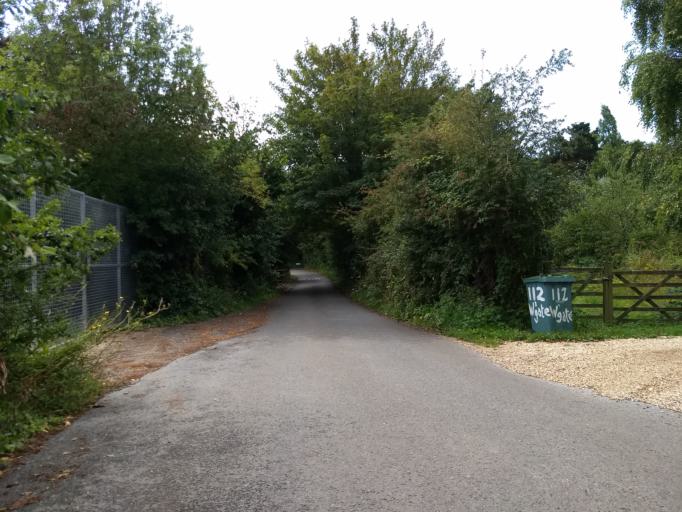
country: GB
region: England
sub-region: Isle of Wight
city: Newport
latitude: 50.6863
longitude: -1.2952
